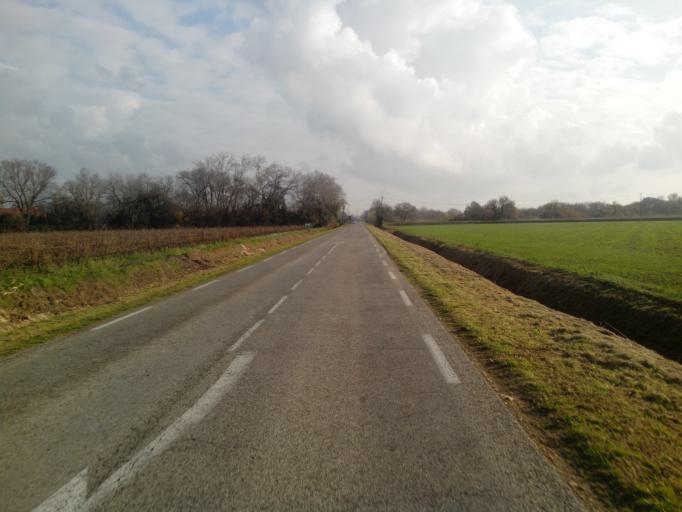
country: FR
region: Provence-Alpes-Cote d'Azur
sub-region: Departement des Bouches-du-Rhone
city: Arles
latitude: 43.5775
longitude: 4.6615
